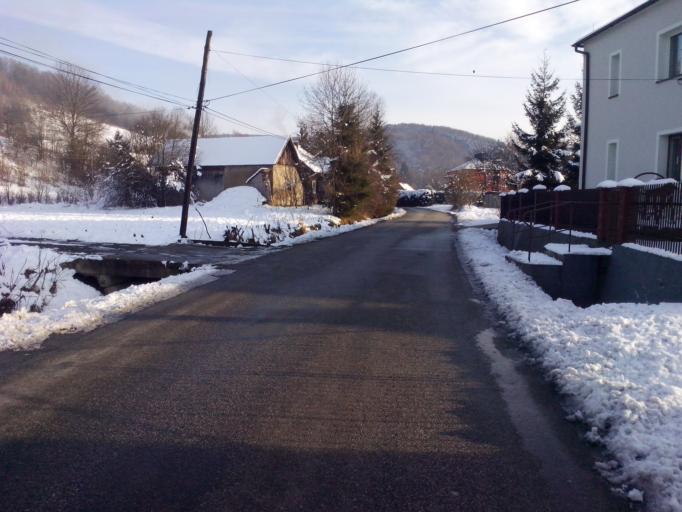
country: PL
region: Subcarpathian Voivodeship
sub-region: Powiat strzyzowski
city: Strzyzow
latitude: 49.8647
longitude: 21.8275
